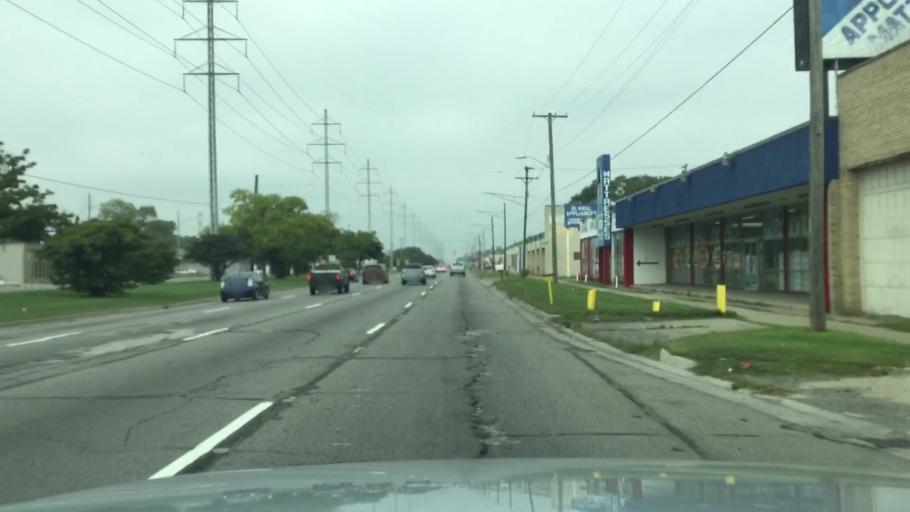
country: US
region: Michigan
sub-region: Macomb County
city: Eastpointe
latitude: 42.4495
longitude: -82.9911
